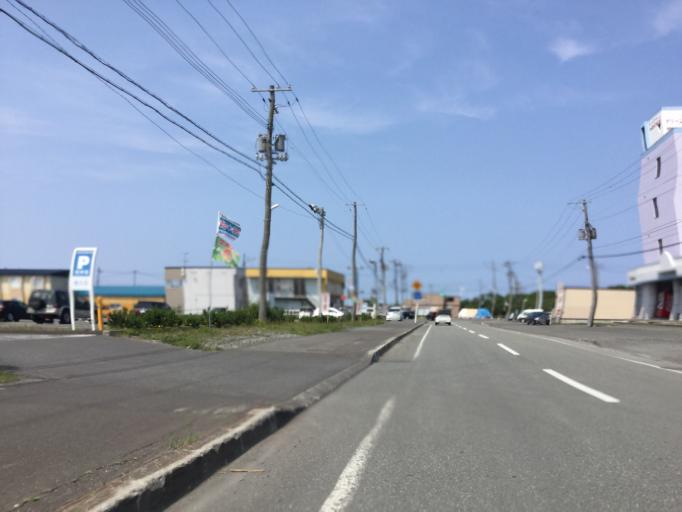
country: JP
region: Hokkaido
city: Wakkanai
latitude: 45.3853
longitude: 141.7042
